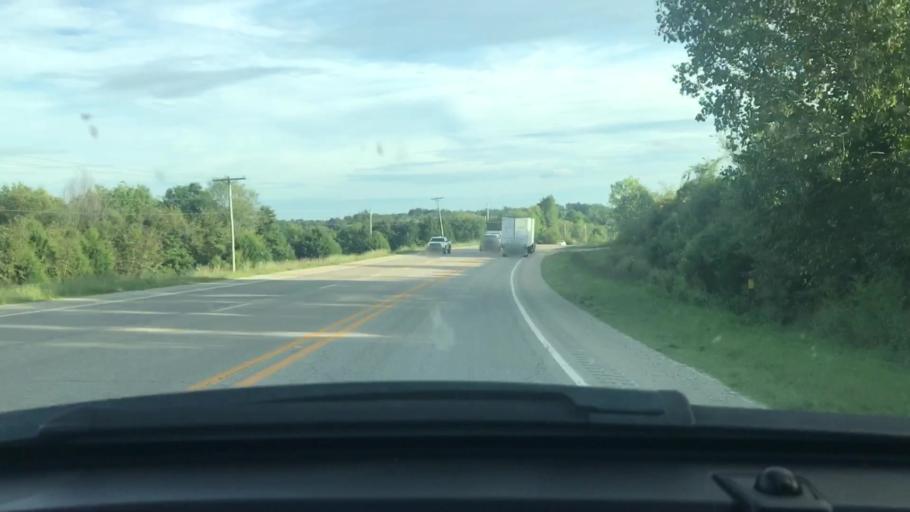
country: US
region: Arkansas
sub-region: Lawrence County
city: Hoxie
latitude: 36.1436
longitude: -91.1583
